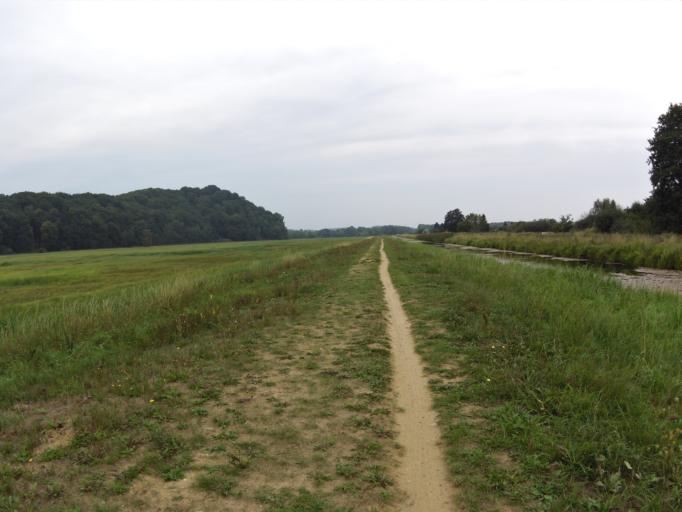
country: PL
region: West Pomeranian Voivodeship
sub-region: Swinoujscie
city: Swinoujscie
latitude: 53.8811
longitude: 14.2151
